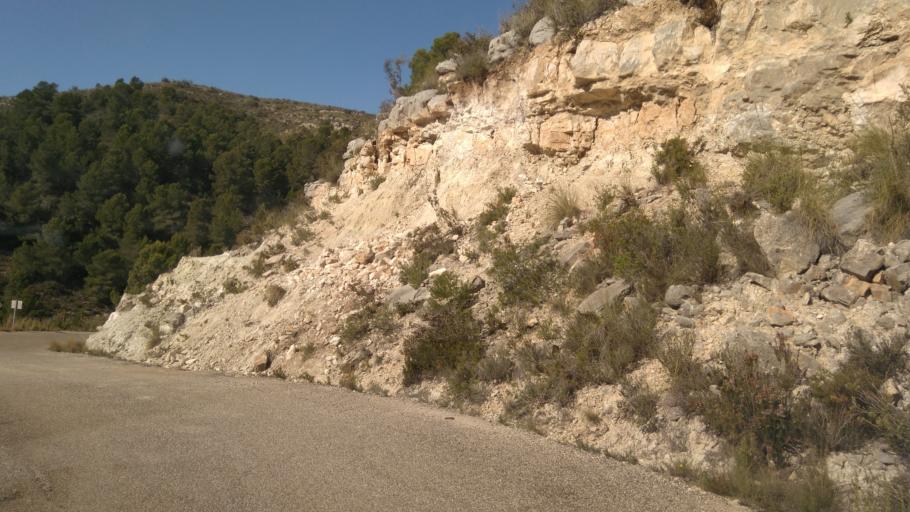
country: ES
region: Valencia
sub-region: Provincia de Valencia
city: Sumacarcer
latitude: 39.1538
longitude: -0.6499
